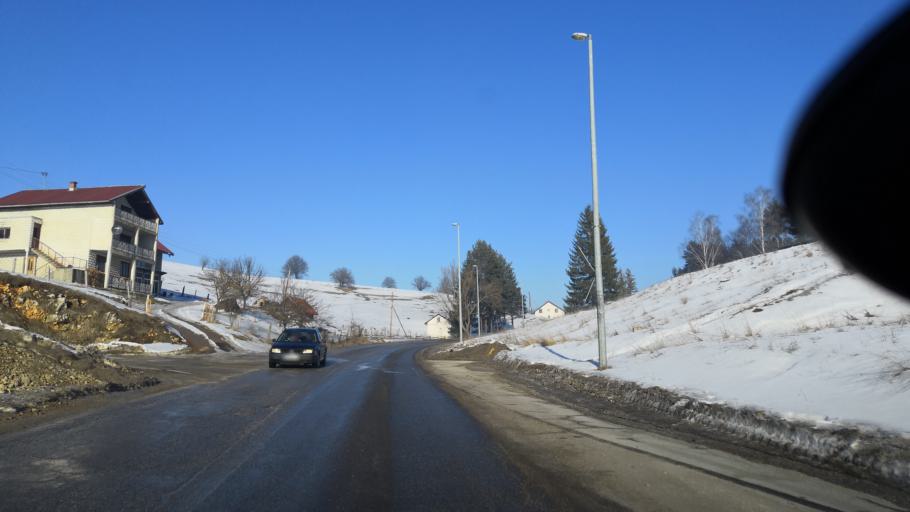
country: BA
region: Republika Srpska
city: Sokolac
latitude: 43.9192
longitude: 18.7702
